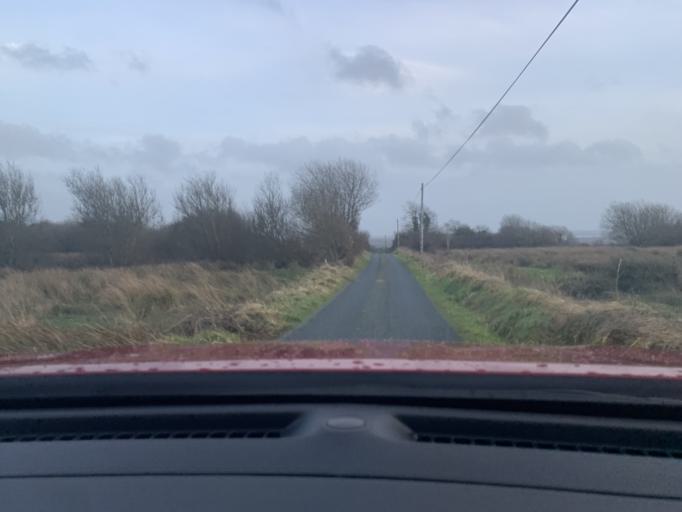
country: IE
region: Connaught
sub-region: Roscommon
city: Ballaghaderreen
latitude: 53.9456
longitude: -8.5026
